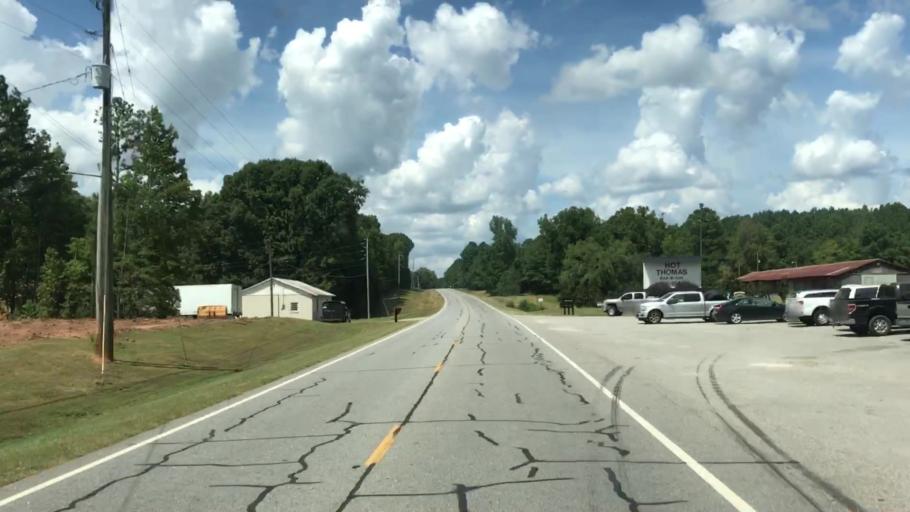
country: US
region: Georgia
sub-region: Oconee County
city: Watkinsville
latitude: 33.8061
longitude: -83.3462
